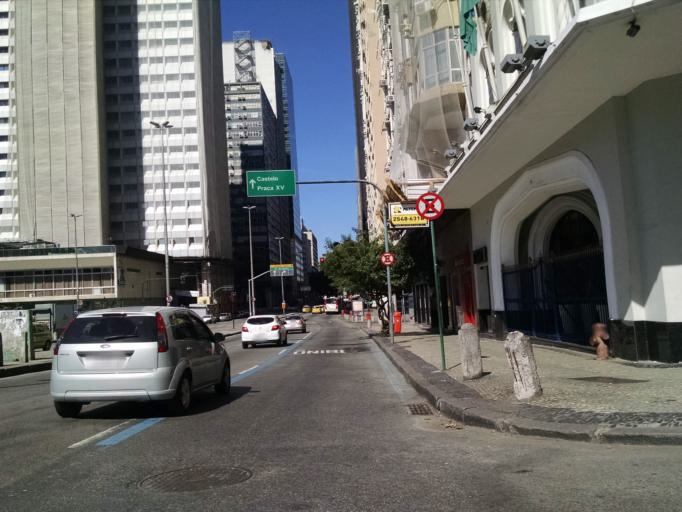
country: BR
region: Rio de Janeiro
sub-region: Rio De Janeiro
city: Rio de Janeiro
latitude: -22.9086
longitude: -43.1784
